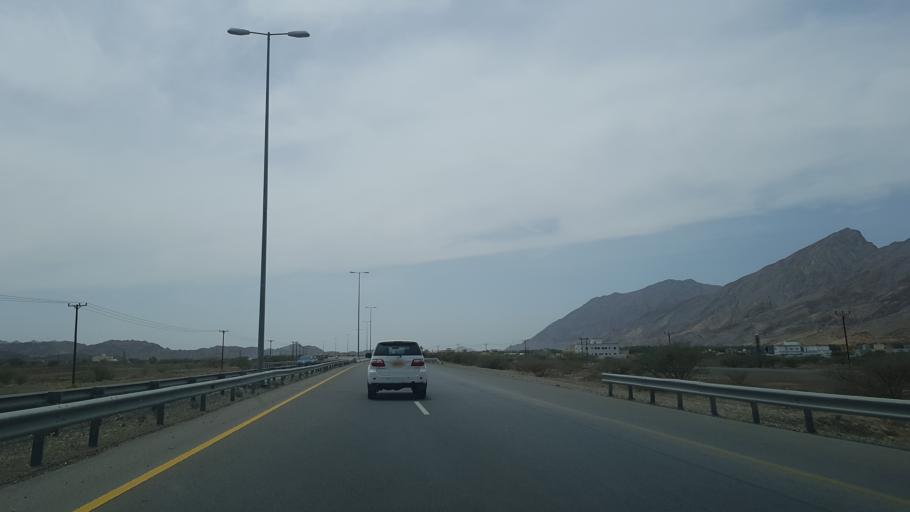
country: OM
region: Muhafazat ad Dakhiliyah
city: Izki
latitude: 23.0170
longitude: 57.7930
